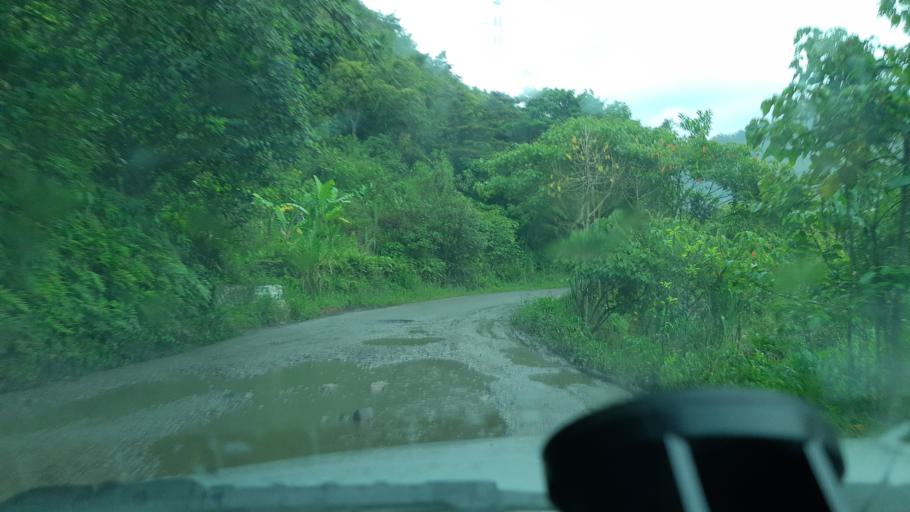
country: CO
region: Boyaca
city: Chinavita
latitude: 5.2021
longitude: -73.3876
